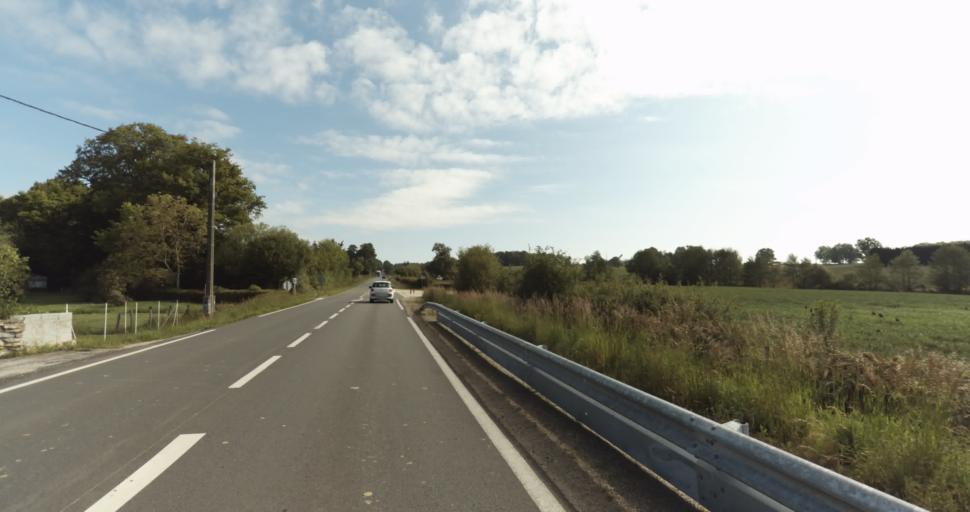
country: FR
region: Limousin
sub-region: Departement de la Haute-Vienne
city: Solignac
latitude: 45.7084
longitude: 1.2425
